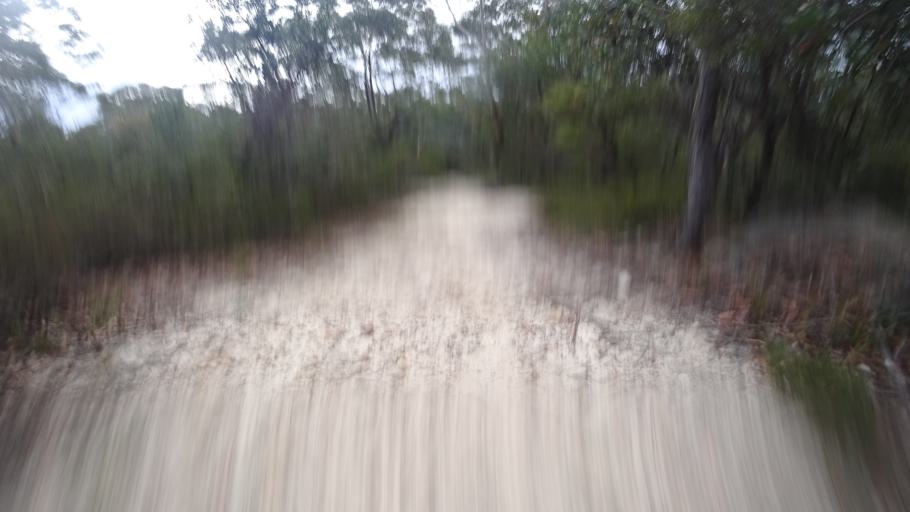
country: AU
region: New South Wales
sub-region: Warringah
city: Davidson
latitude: -33.6888
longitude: 151.1983
